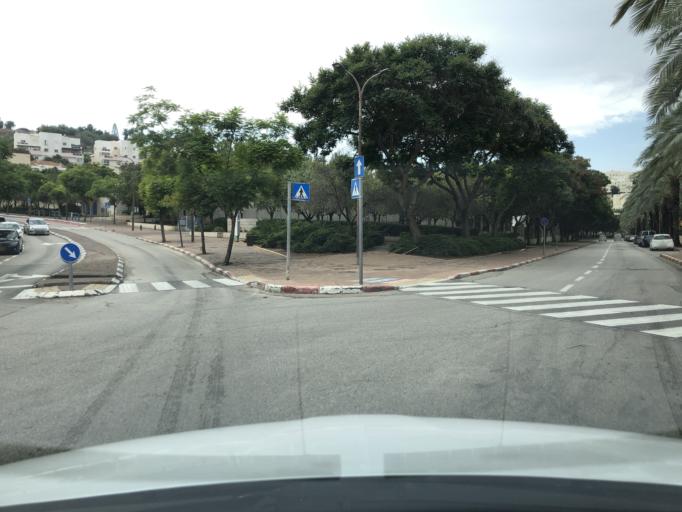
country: IL
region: Central District
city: Modiin
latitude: 31.8969
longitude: 35.0155
